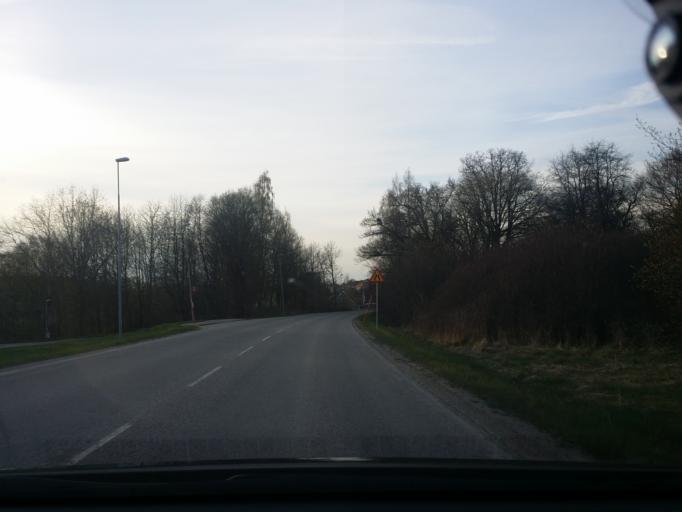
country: SE
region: Uppsala
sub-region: Enkopings Kommun
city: Enkoping
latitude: 59.6360
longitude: 17.1030
